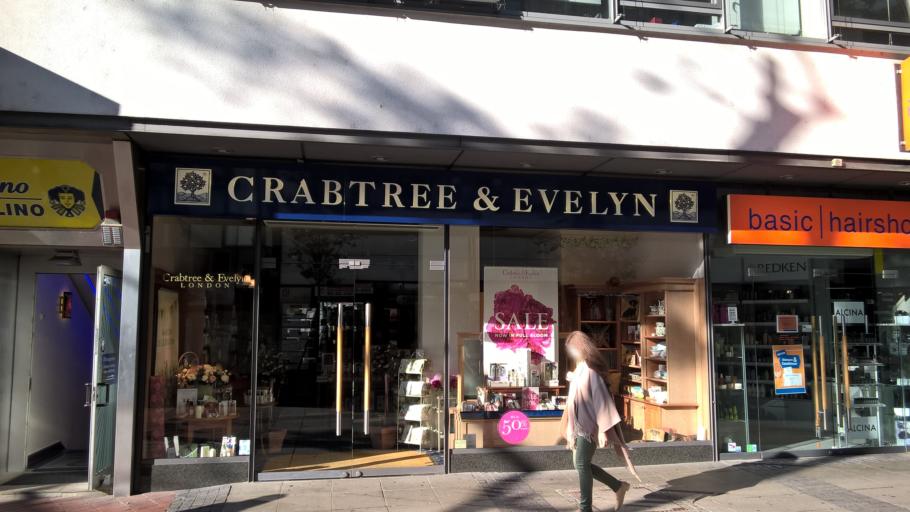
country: DE
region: Baden-Wuerttemberg
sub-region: Regierungsbezirk Stuttgart
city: Stuttgart
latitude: 48.7769
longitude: 9.1751
